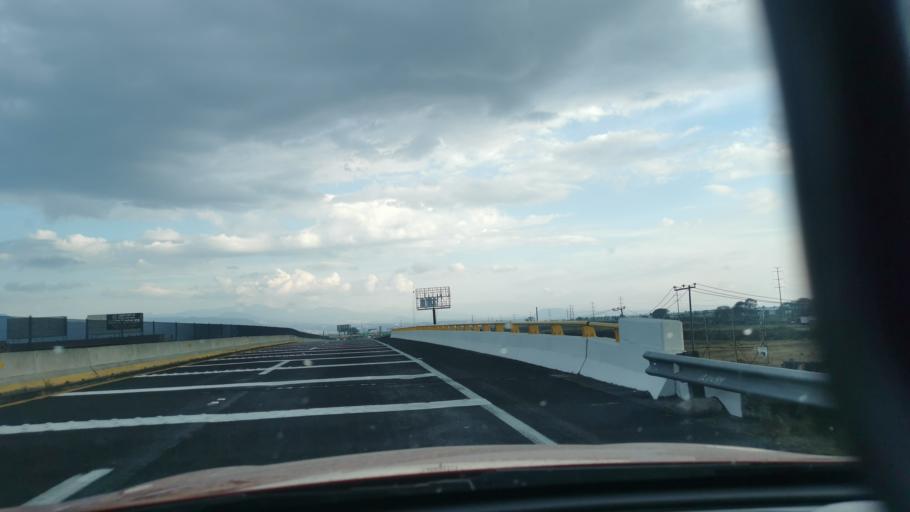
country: MX
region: Mexico
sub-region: Toluca
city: San Nicolas Tolentino
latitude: 19.3797
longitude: -99.5536
